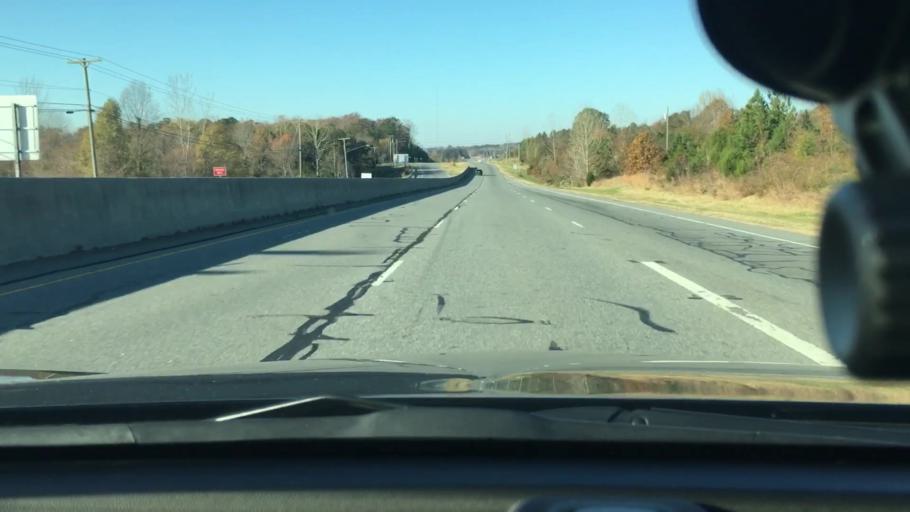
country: US
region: North Carolina
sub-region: Cabarrus County
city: Concord
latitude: 35.3729
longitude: -80.5537
